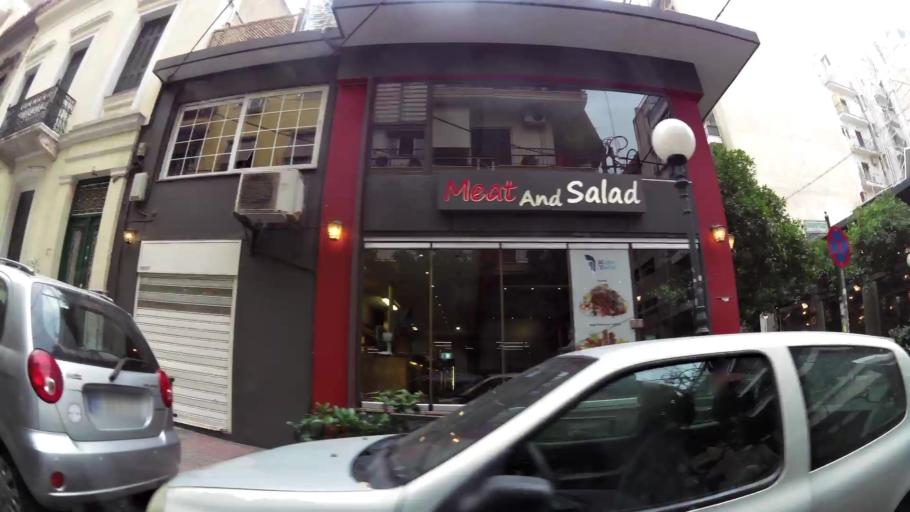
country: GR
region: Attica
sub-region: Nomos Attikis
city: Piraeus
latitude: 37.9425
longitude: 23.6505
